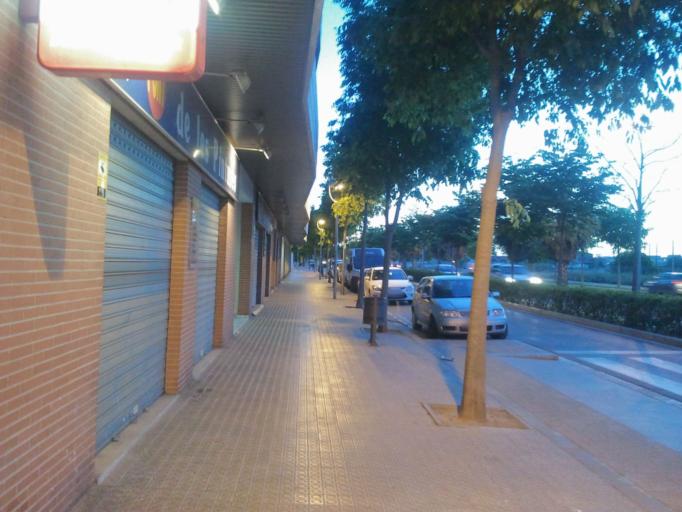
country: ES
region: Catalonia
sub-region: Provincia de Barcelona
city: Vilanova i la Geltru
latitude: 41.2279
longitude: 1.7182
